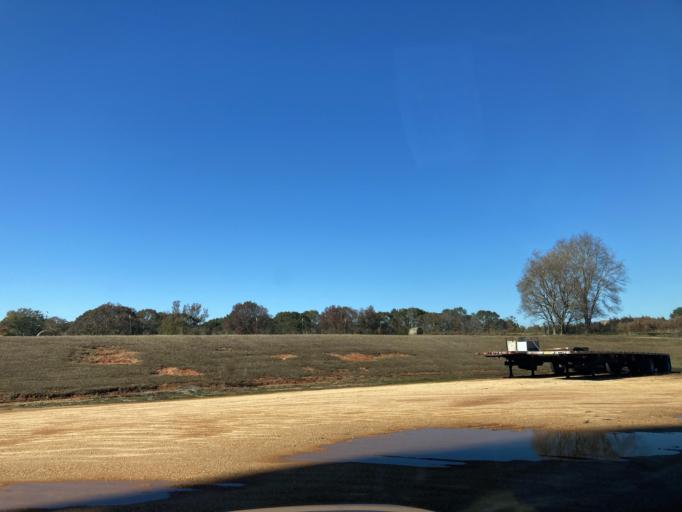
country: US
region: Mississippi
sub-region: Lamar County
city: Sumrall
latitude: 31.2943
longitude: -89.5758
